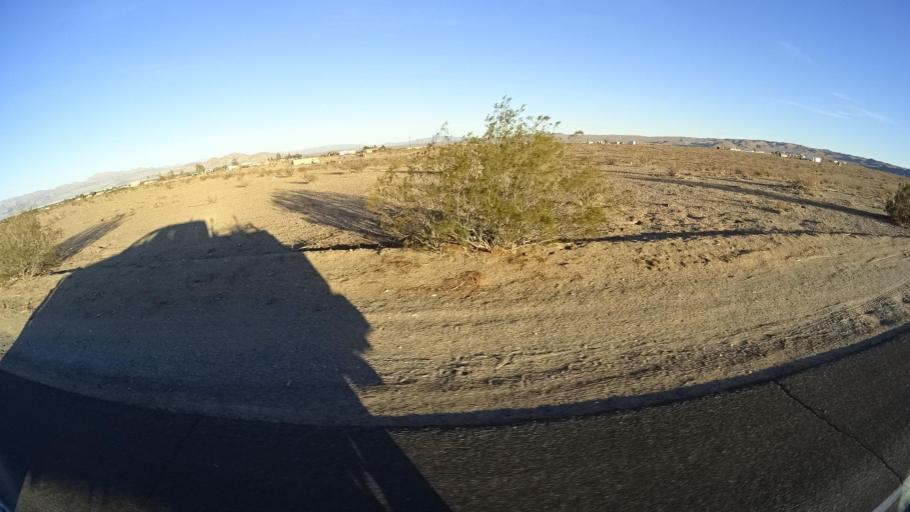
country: US
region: California
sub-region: Kern County
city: China Lake Acres
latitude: 35.6130
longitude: -117.7230
